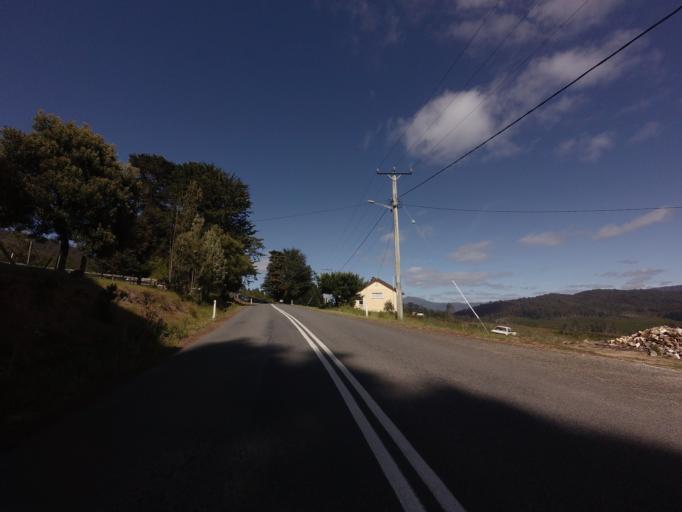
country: AU
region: Tasmania
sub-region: Derwent Valley
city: New Norfolk
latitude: -42.7487
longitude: 146.6474
